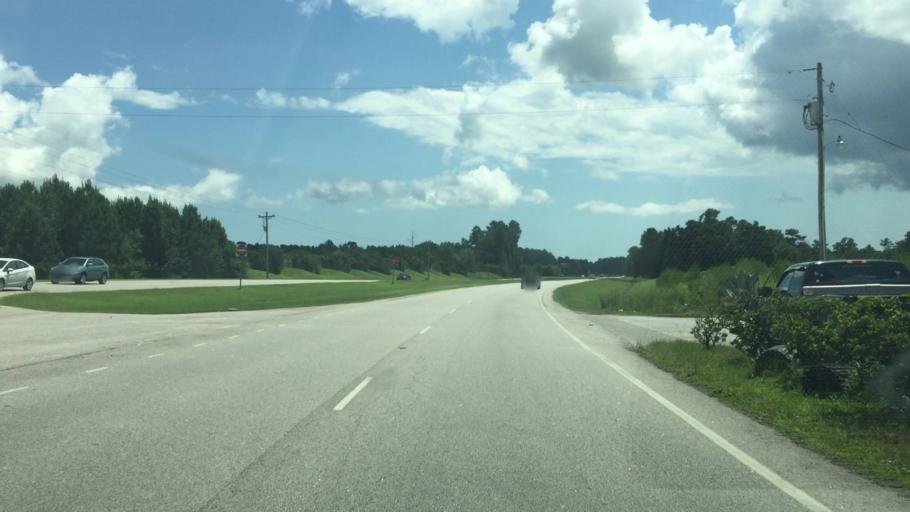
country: US
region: South Carolina
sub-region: Horry County
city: Little River
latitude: 33.9547
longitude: -78.7357
